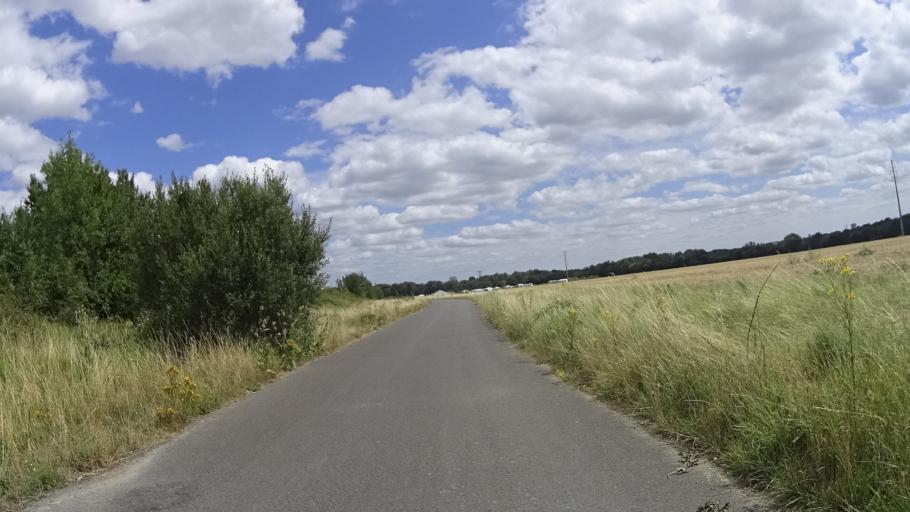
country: FR
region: Centre
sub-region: Departement d'Indre-et-Loire
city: La Riche
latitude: 47.3734
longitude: 0.6541
